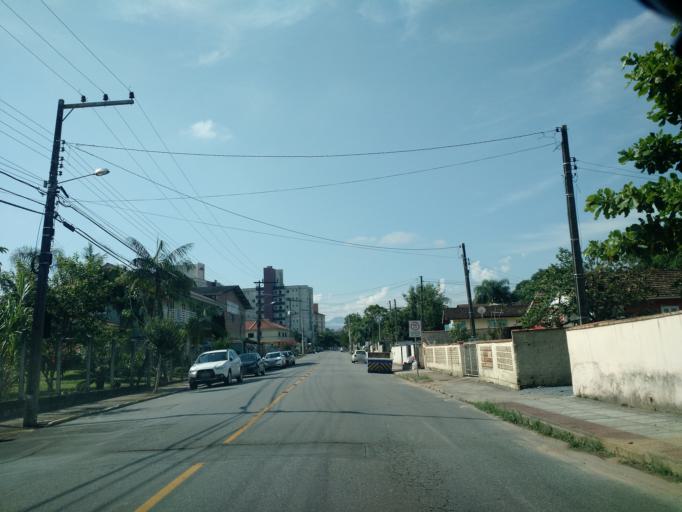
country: BR
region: Santa Catarina
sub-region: Jaragua Do Sul
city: Jaragua do Sul
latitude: -26.5030
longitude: -49.0961
